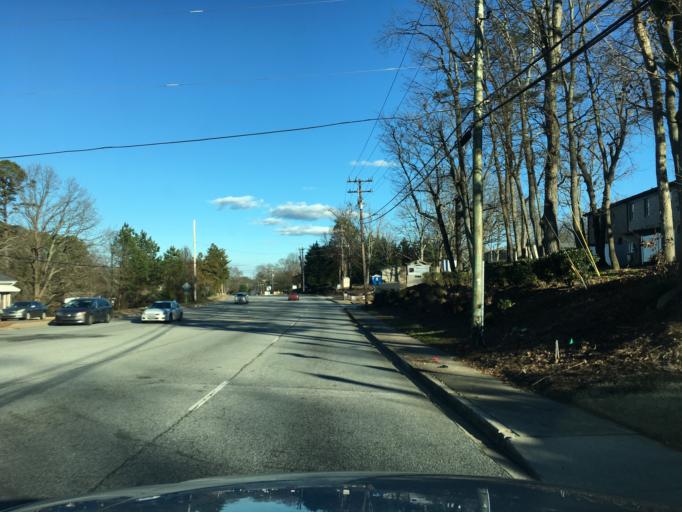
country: US
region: South Carolina
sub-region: Greenville County
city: Wade Hampton
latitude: 34.8704
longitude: -82.3468
